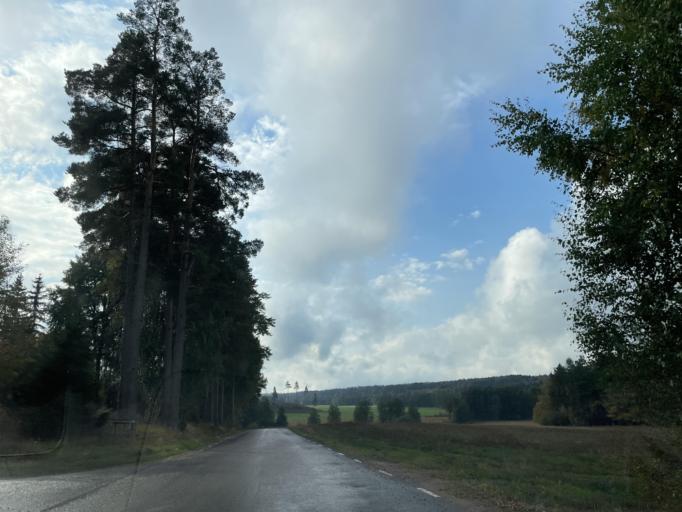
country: SE
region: Vaermland
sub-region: Karlstads Kommun
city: Skattkarr
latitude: 59.4301
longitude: 13.6053
